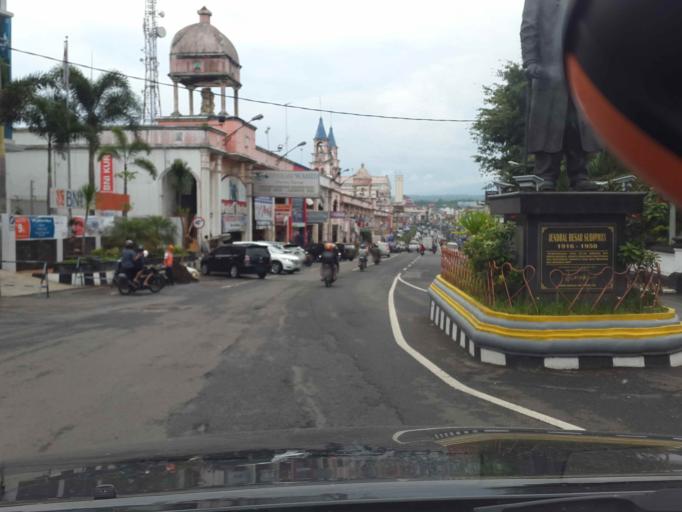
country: ID
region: Central Java
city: Salatiga
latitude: -7.3249
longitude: 110.5049
